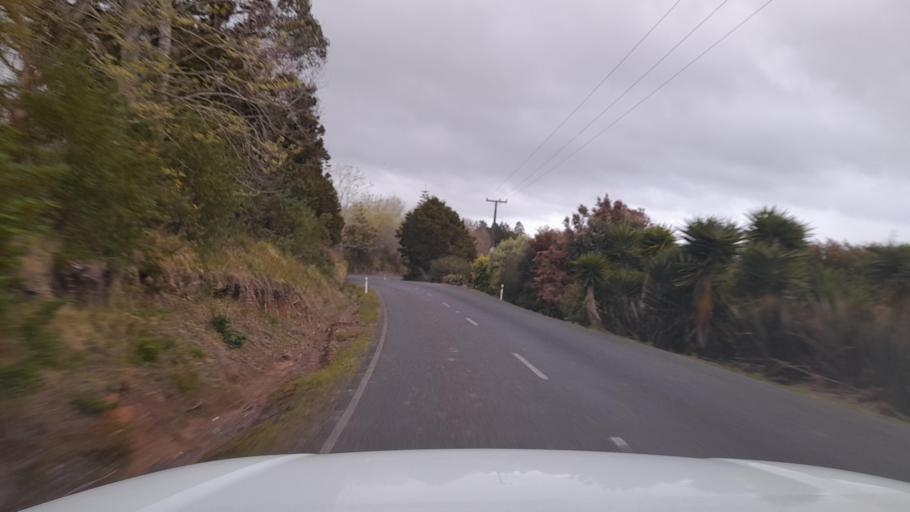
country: NZ
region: Northland
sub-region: Whangarei
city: Maungatapere
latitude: -35.6389
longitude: 174.2150
